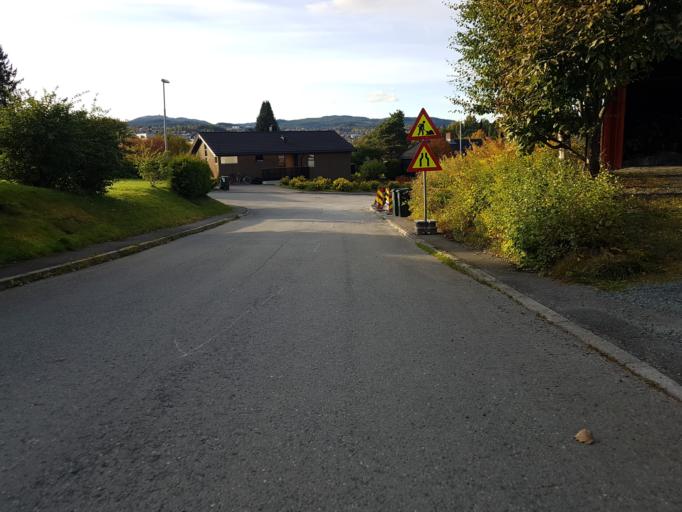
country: NO
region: Sor-Trondelag
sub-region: Trondheim
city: Trondheim
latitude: 63.4005
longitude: 10.4162
